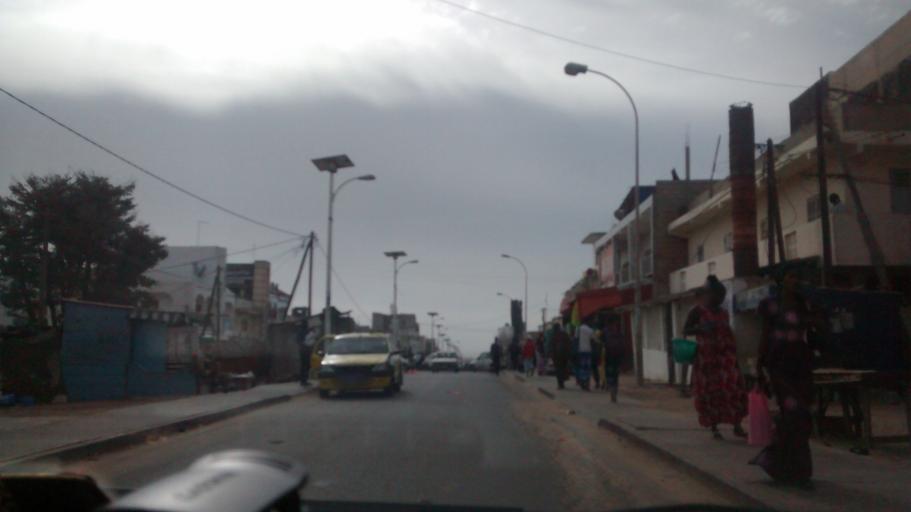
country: SN
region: Dakar
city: Pikine
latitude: 14.7815
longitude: -17.3813
